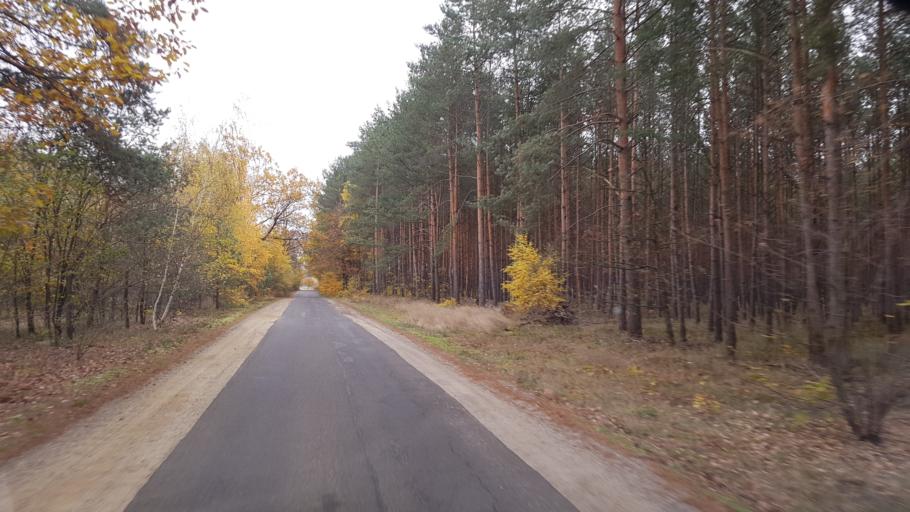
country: DE
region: Brandenburg
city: Crinitz
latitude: 51.7253
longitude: 13.7687
